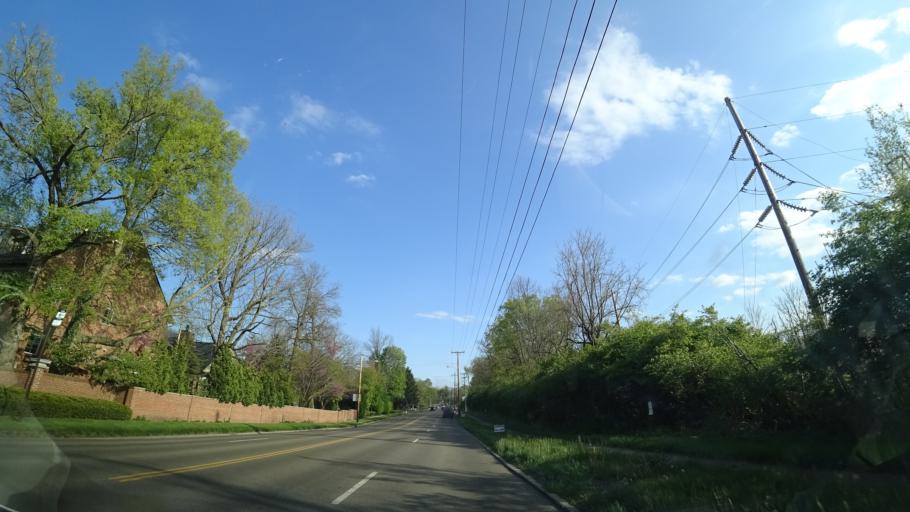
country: US
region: Ohio
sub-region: Montgomery County
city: Oakwood
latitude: 39.7353
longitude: -84.1853
